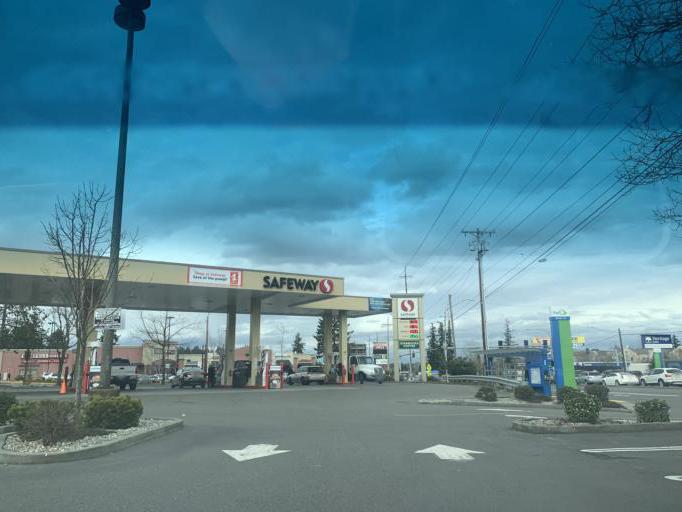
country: US
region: Washington
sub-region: Snohomish County
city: Alderwood Manor
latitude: 47.8637
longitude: -122.2828
